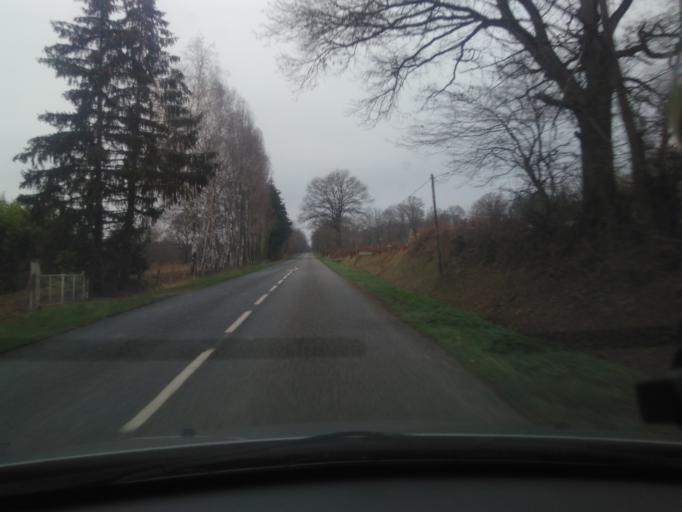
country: FR
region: Centre
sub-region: Departement du Cher
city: Chateaumeillant
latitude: 46.6339
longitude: 2.1787
